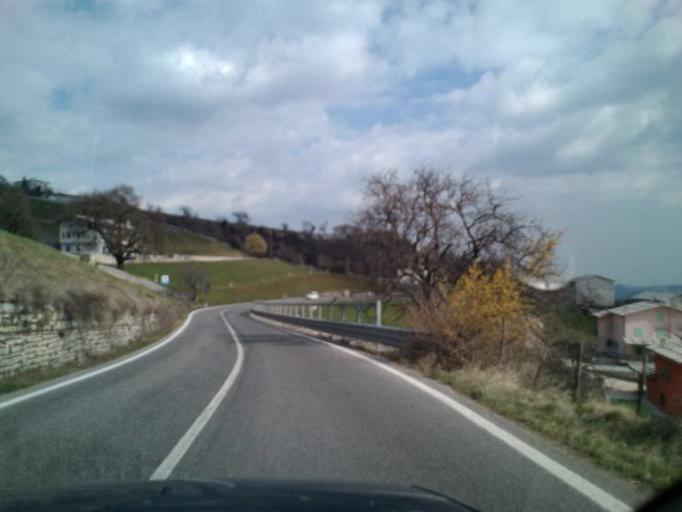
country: IT
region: Veneto
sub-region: Provincia di Verona
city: Sant'Anna d'Alfaedo
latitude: 45.6224
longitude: 10.9455
